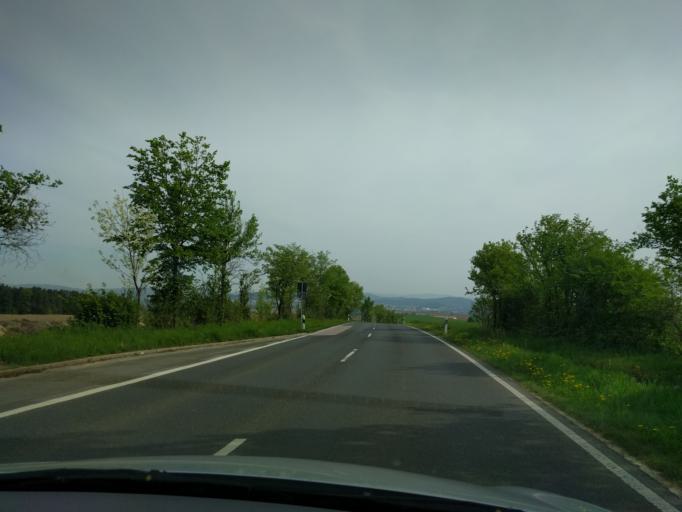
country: DE
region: Bavaria
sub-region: Upper Palatinate
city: Traitsching
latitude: 49.1848
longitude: 12.6352
